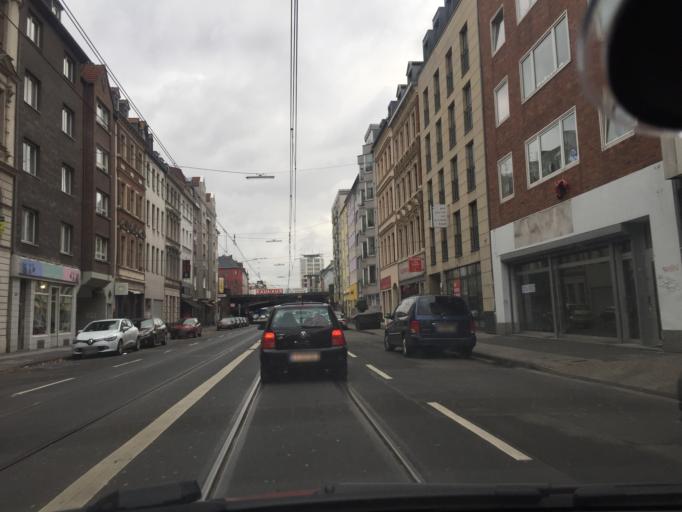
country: DE
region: North Rhine-Westphalia
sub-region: Regierungsbezirk Koln
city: Neustadt/Sued
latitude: 50.9256
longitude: 6.9378
